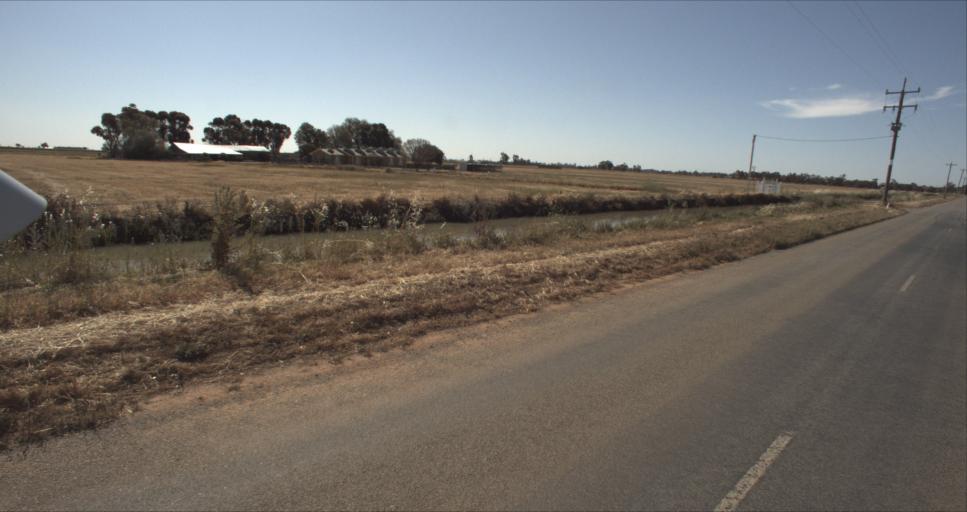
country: AU
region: New South Wales
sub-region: Leeton
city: Leeton
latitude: -34.5780
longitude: 146.3804
